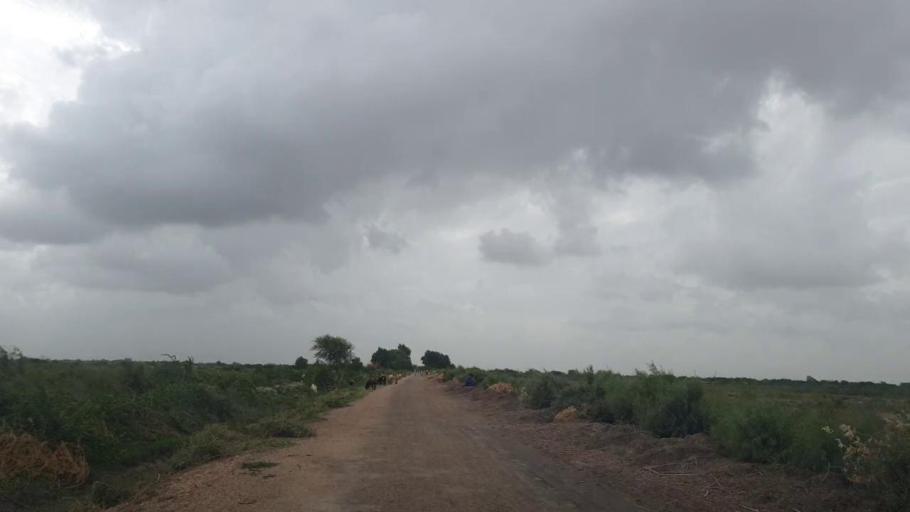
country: PK
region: Sindh
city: Tando Bago
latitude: 24.8483
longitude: 69.1604
